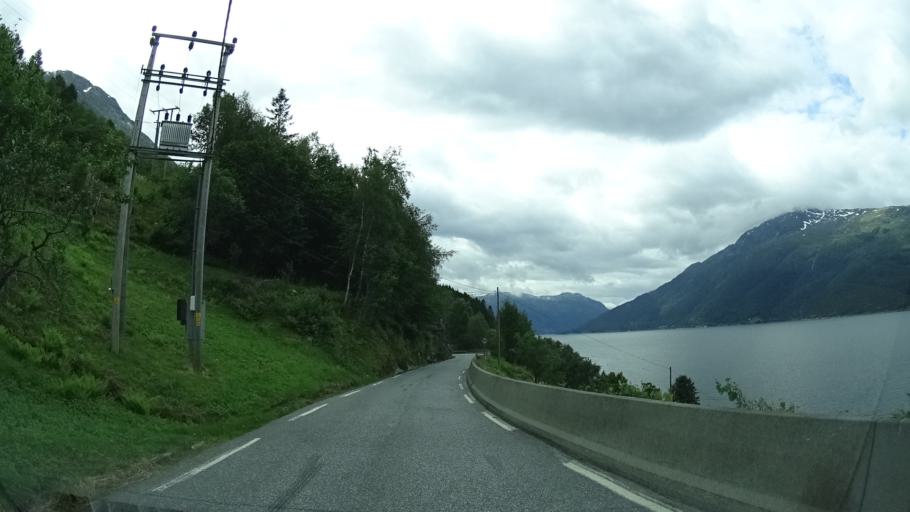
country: NO
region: Hordaland
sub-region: Ullensvang
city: Kinsarvik
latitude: 60.4491
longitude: 6.8022
